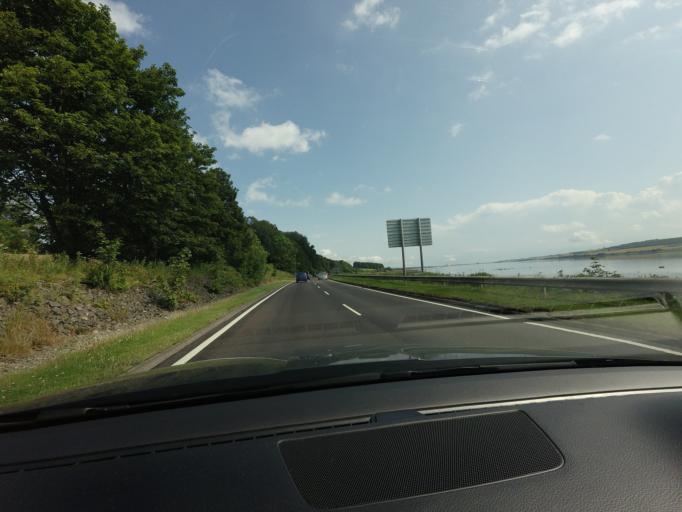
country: GB
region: Scotland
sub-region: Highland
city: Evanton
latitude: 57.6308
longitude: -4.3659
